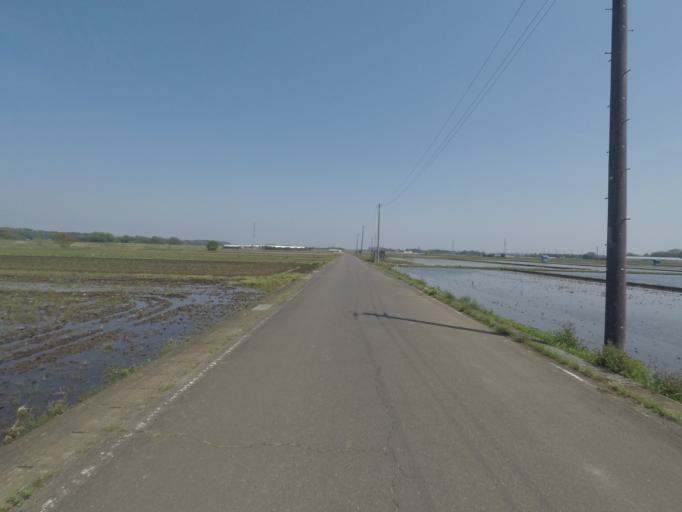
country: JP
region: Ibaraki
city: Naka
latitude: 36.1019
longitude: 140.1556
